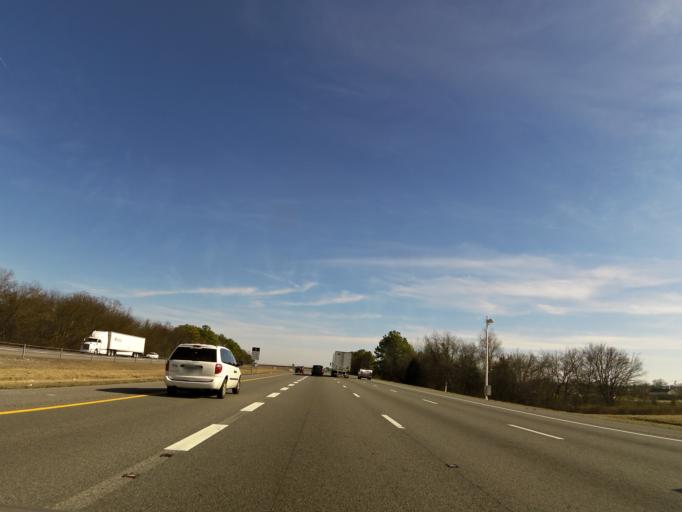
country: US
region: Tennessee
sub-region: Rutherford County
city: Smyrna
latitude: 35.8929
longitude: -86.4857
